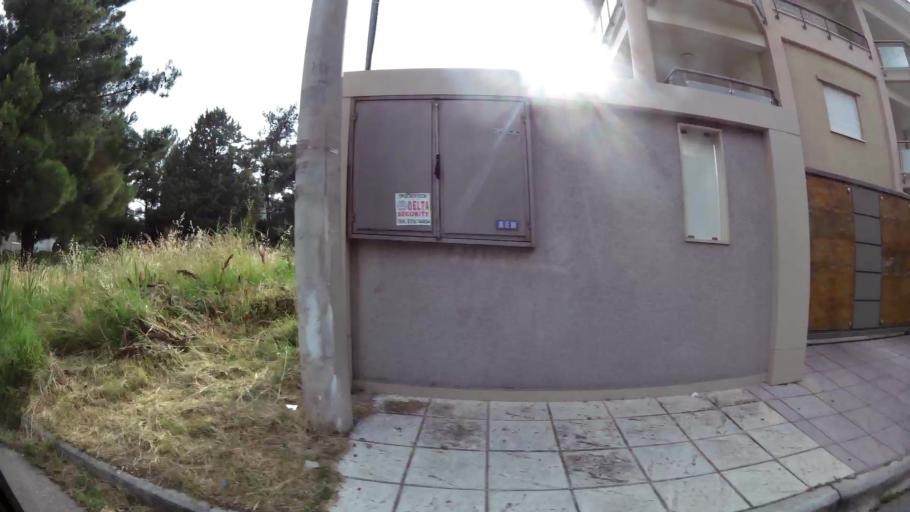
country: GR
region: Central Macedonia
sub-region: Nomos Thessalonikis
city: Oraiokastro
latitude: 40.7288
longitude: 22.9204
